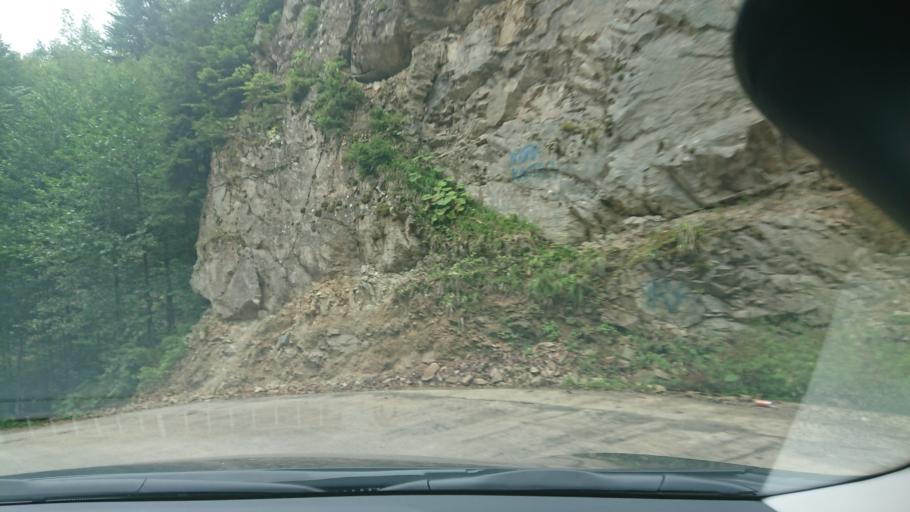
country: TR
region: Gumushane
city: Kurtun
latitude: 40.6606
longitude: 39.0262
